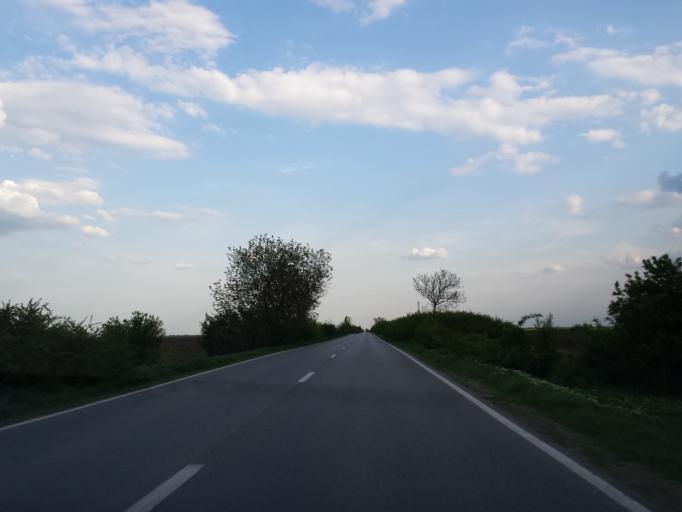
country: RO
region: Timis
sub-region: Comuna Tomnatic
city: Tomnatic
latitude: 45.9902
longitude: 20.6919
